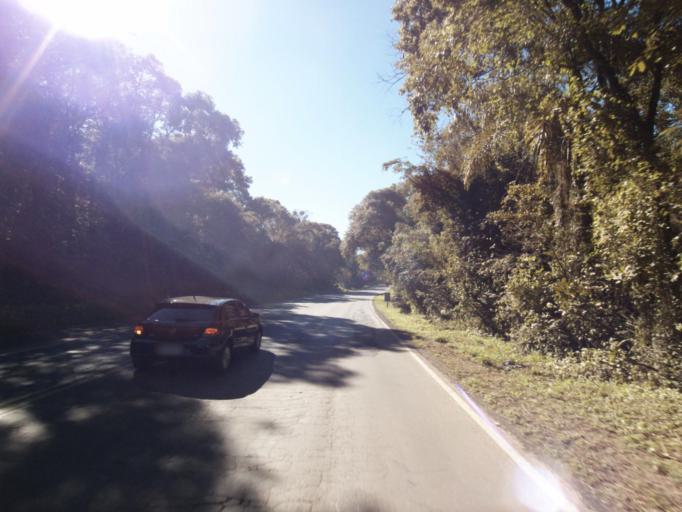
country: BR
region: Rio Grande do Sul
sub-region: Frederico Westphalen
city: Frederico Westphalen
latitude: -26.7972
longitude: -53.3054
